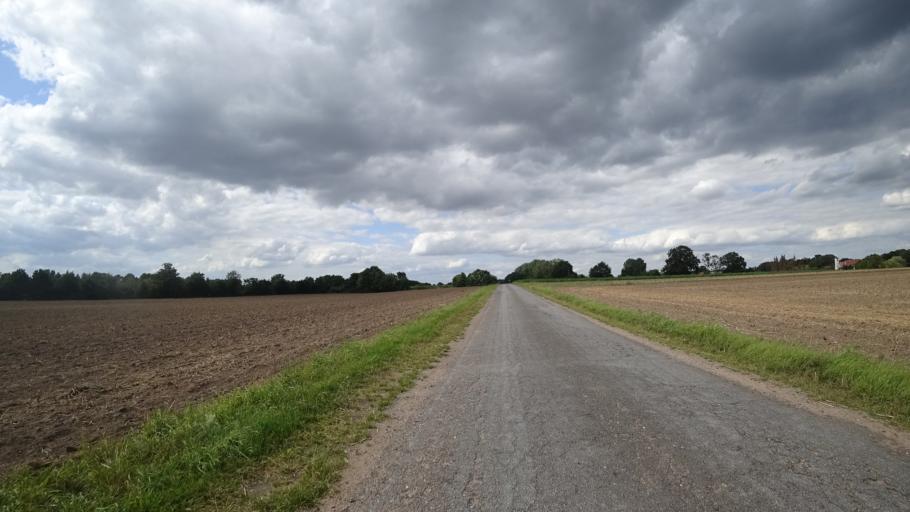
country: DE
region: Lower Saxony
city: Raddestorf
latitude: 52.4267
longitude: 9.0326
